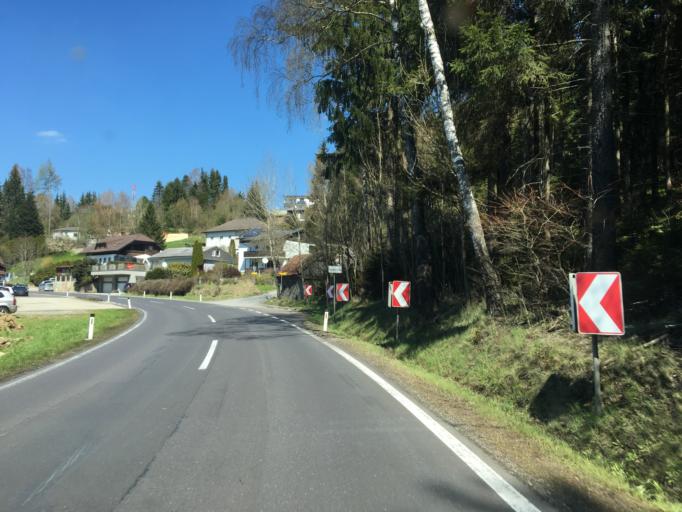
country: AT
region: Upper Austria
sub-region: Politischer Bezirk Urfahr-Umgebung
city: Sonnberg im Muehlkreis
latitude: 48.4812
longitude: 14.2979
